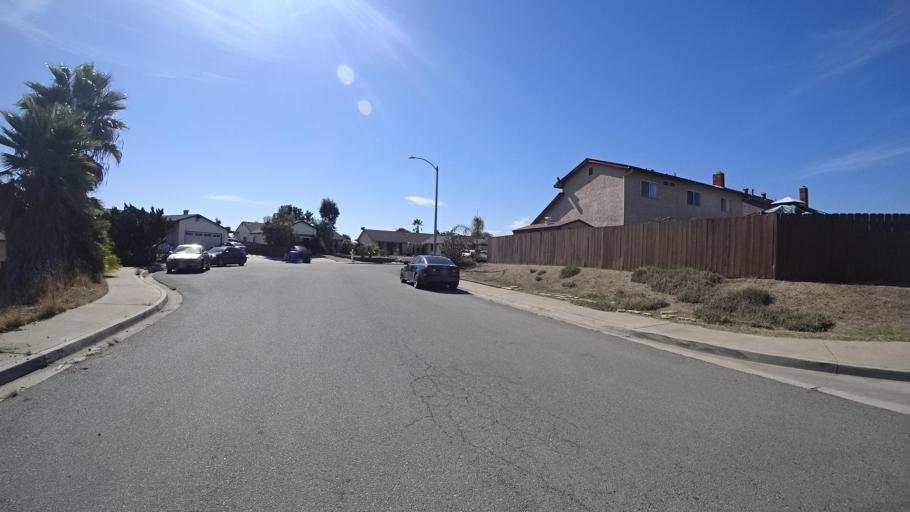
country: US
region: California
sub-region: San Diego County
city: La Presa
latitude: 32.7052
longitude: -116.9919
